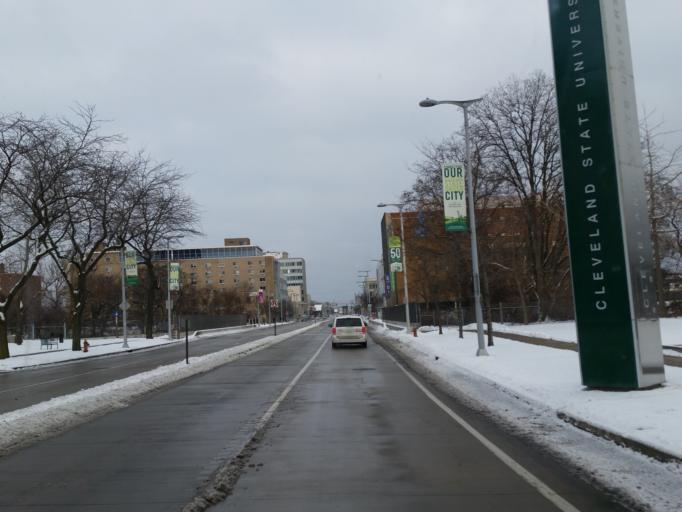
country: US
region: Ohio
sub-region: Cuyahoga County
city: Cleveland
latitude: 41.5020
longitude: -81.6710
